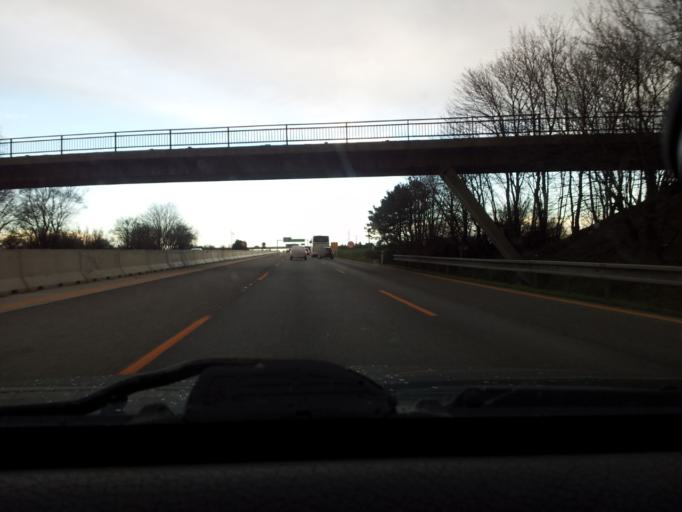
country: SK
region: Trnavsky
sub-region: Okres Trnava
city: Trnava
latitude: 48.3324
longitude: 17.6220
